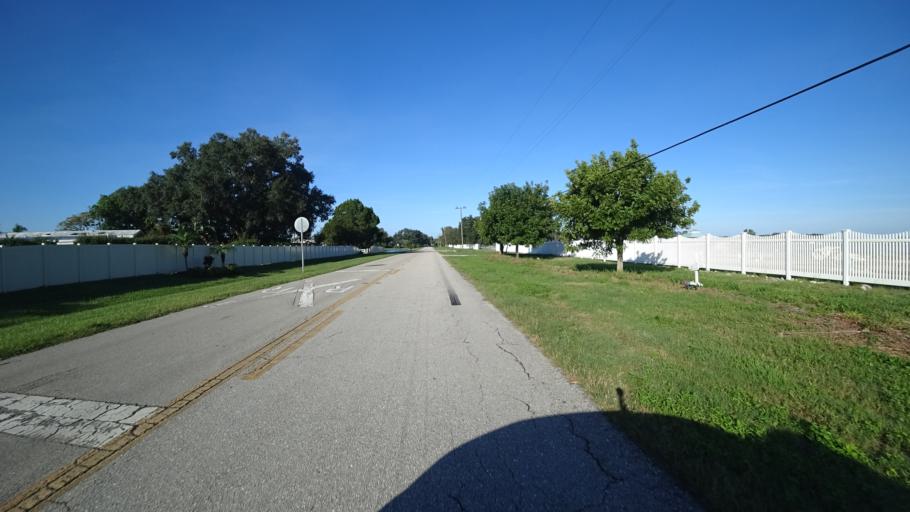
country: US
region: Florida
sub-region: Manatee County
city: Memphis
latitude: 27.5682
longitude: -82.5516
